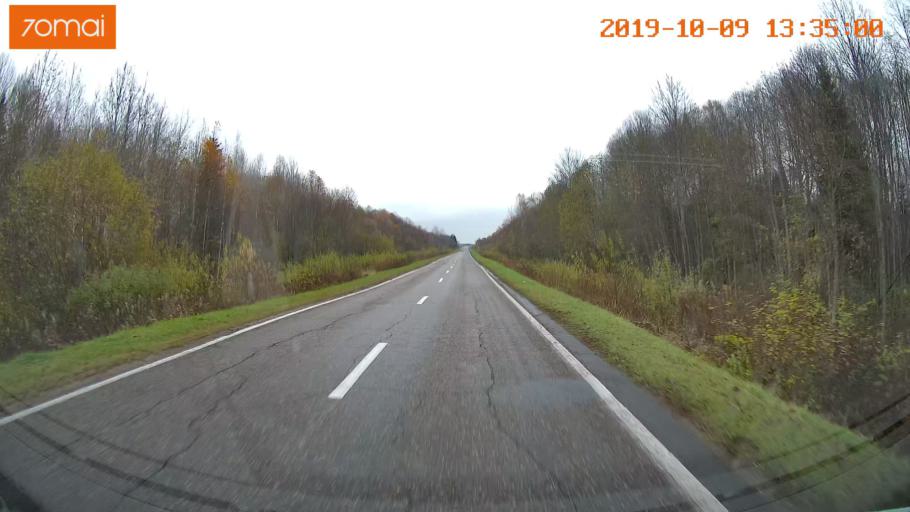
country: RU
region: Jaroslavl
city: Lyubim
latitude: 58.3333
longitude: 41.0698
